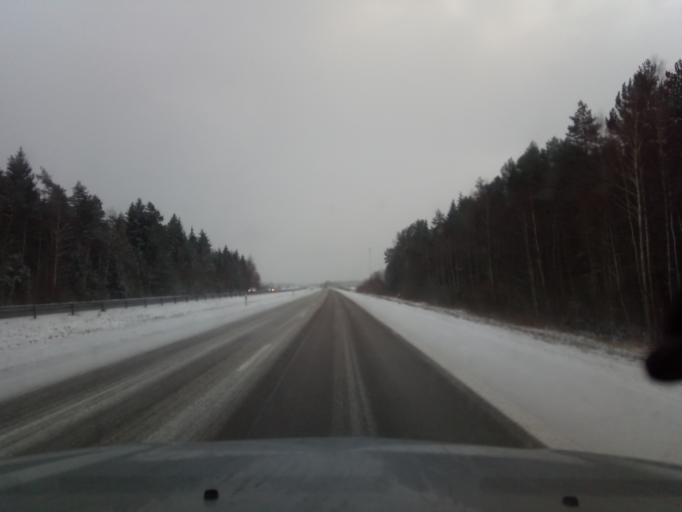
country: LT
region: Vilnius County
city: Ukmerge
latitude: 55.4922
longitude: 24.6261
